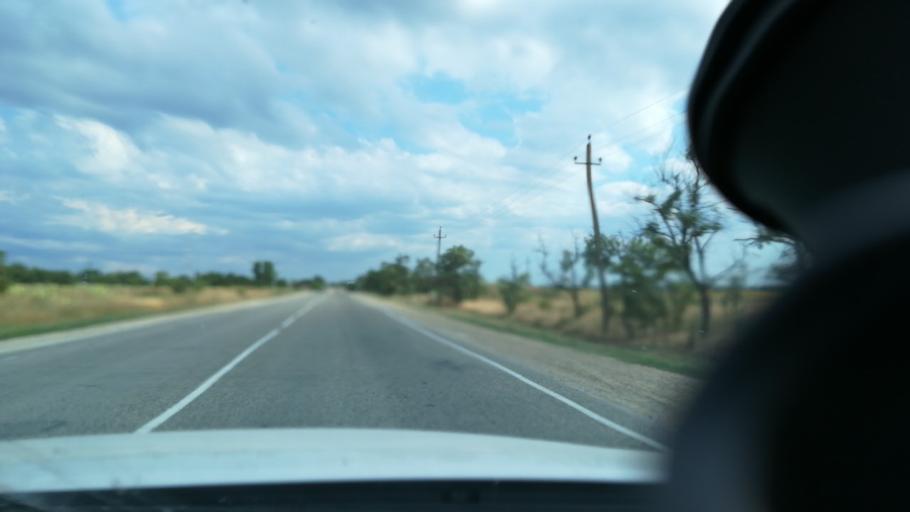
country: RU
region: Krasnodarskiy
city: Yurovka
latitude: 45.0981
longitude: 37.4303
